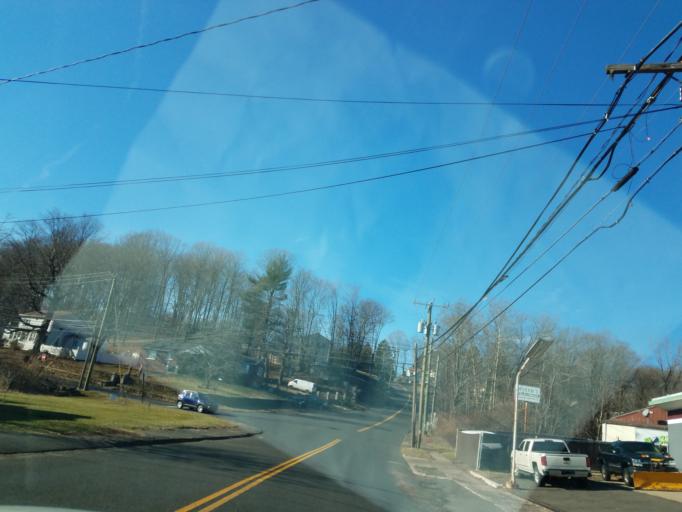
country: US
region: Connecticut
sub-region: New Haven County
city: Meriden
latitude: 41.5412
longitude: -72.8255
